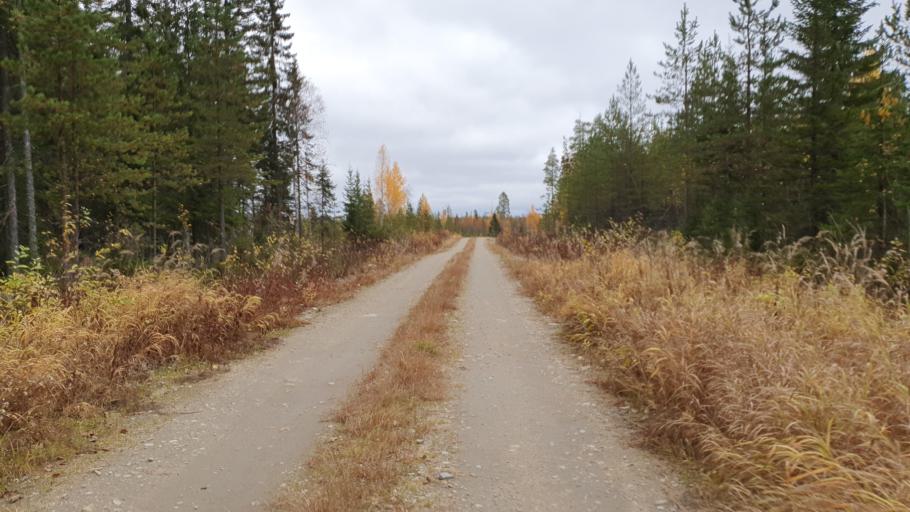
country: FI
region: Kainuu
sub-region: Kehys-Kainuu
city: Kuhmo
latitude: 64.4494
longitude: 29.6086
